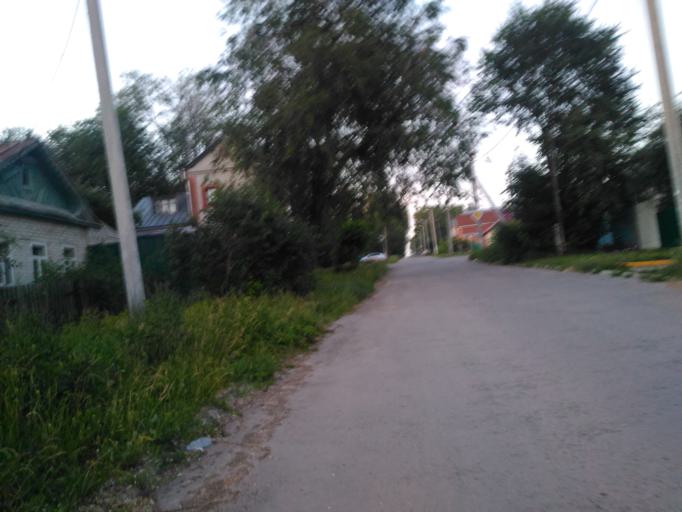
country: RU
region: Ulyanovsk
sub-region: Ulyanovskiy Rayon
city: Ulyanovsk
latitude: 54.3384
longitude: 48.3688
